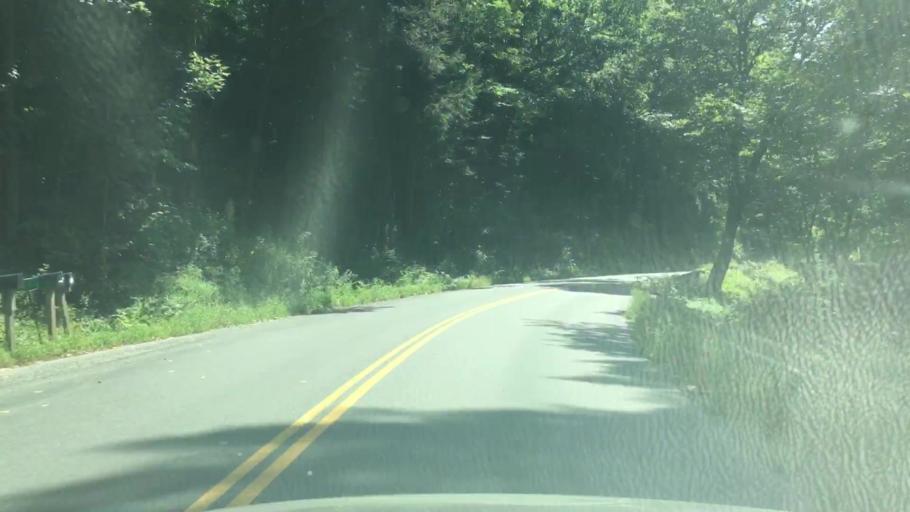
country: US
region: Vermont
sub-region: Windham County
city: West Brattleboro
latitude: 42.8040
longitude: -72.6049
